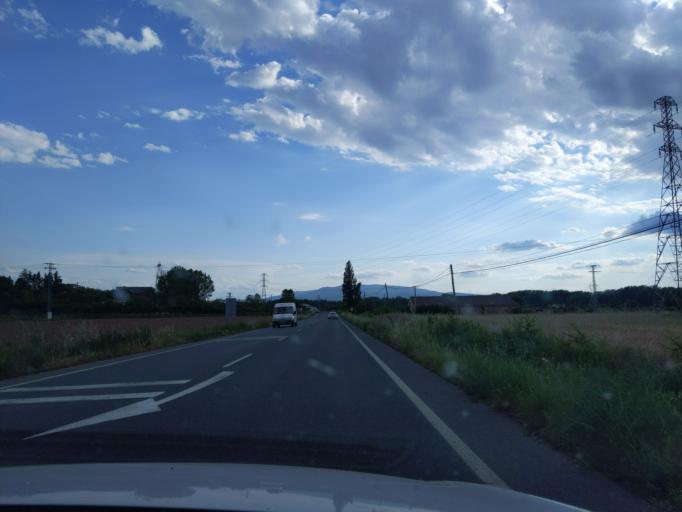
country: ES
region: La Rioja
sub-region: Provincia de La Rioja
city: Villamediana de Iregua
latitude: 42.4218
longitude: -2.4270
